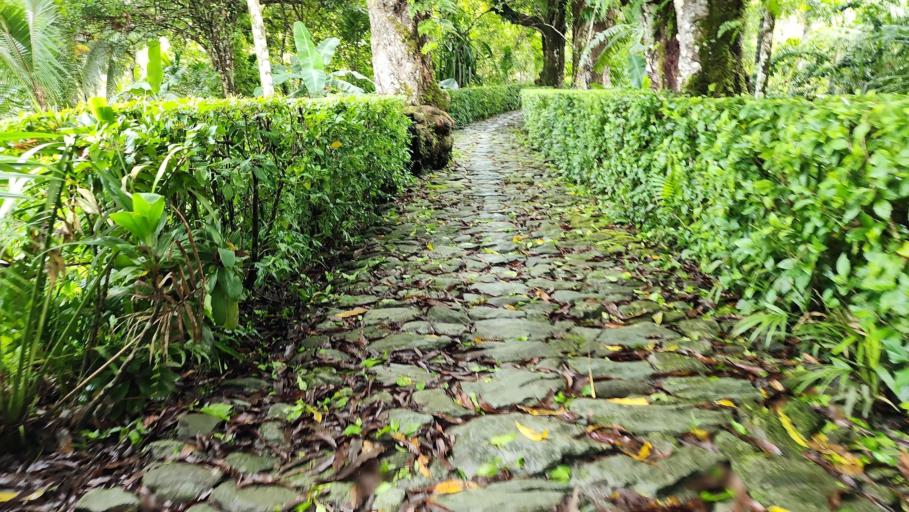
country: FM
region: Yap
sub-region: Weloy Municipality
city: Colonia
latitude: 9.5193
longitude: 138.1198
